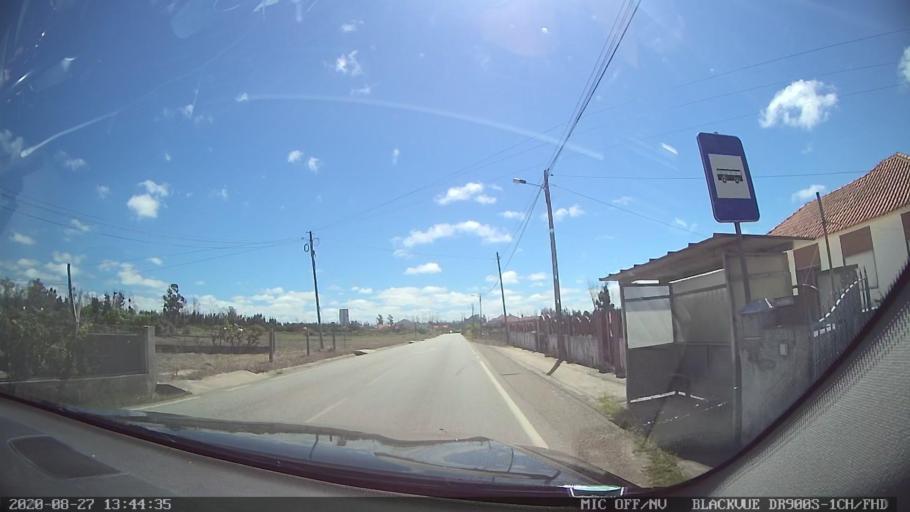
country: PT
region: Coimbra
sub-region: Mira
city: Mira
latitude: 40.4130
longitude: -8.7353
